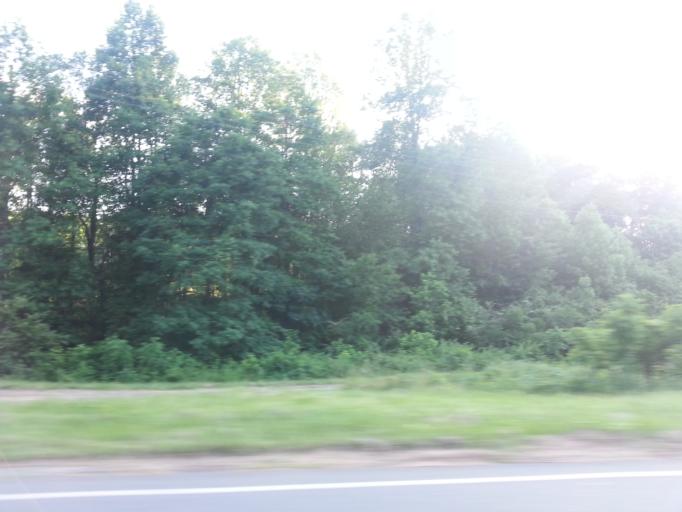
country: US
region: North Carolina
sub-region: Cherokee County
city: Murphy
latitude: 35.0322
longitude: -84.1405
